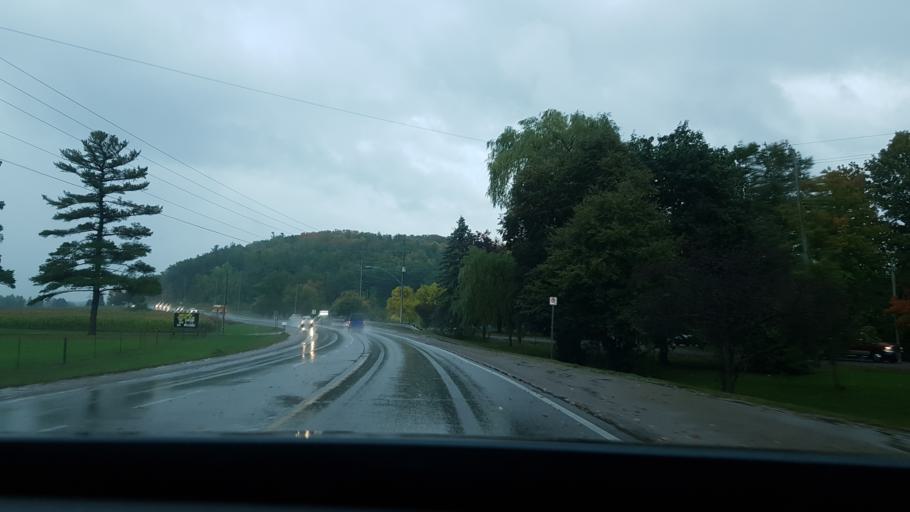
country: CA
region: Ontario
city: Peterborough
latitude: 44.3747
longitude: -78.3865
